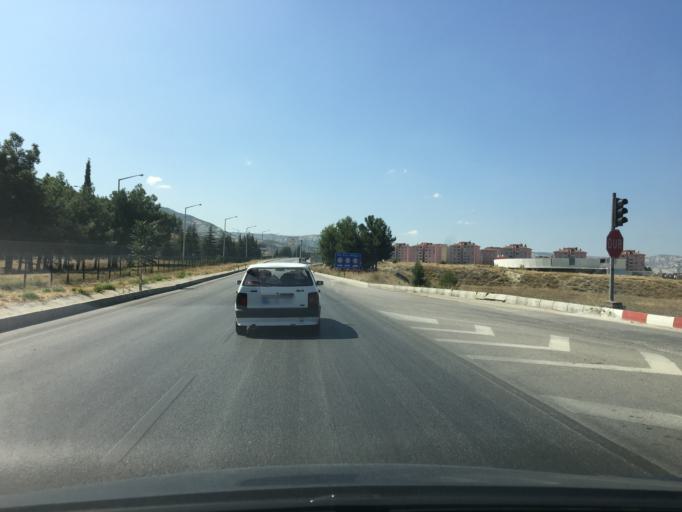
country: TR
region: Burdur
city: Burdur
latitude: 37.7403
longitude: 30.3123
